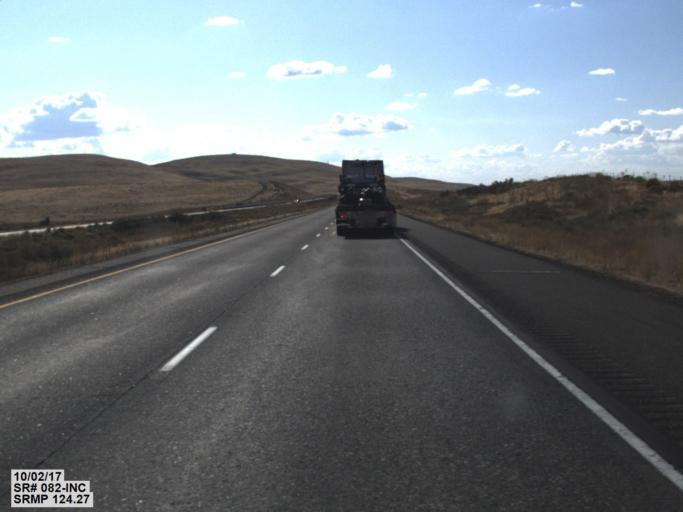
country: US
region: Oregon
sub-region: Umatilla County
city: Umatilla
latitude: 46.0079
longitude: -119.2412
